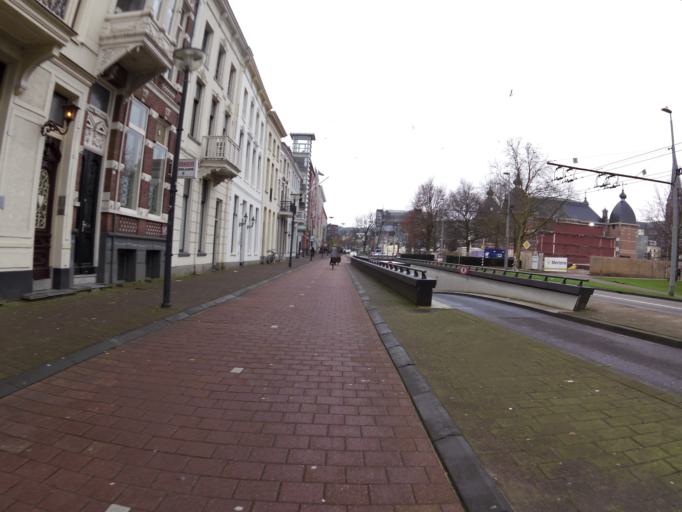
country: NL
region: Gelderland
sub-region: Gemeente Arnhem
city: Arnhem
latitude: 51.9814
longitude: 5.9135
